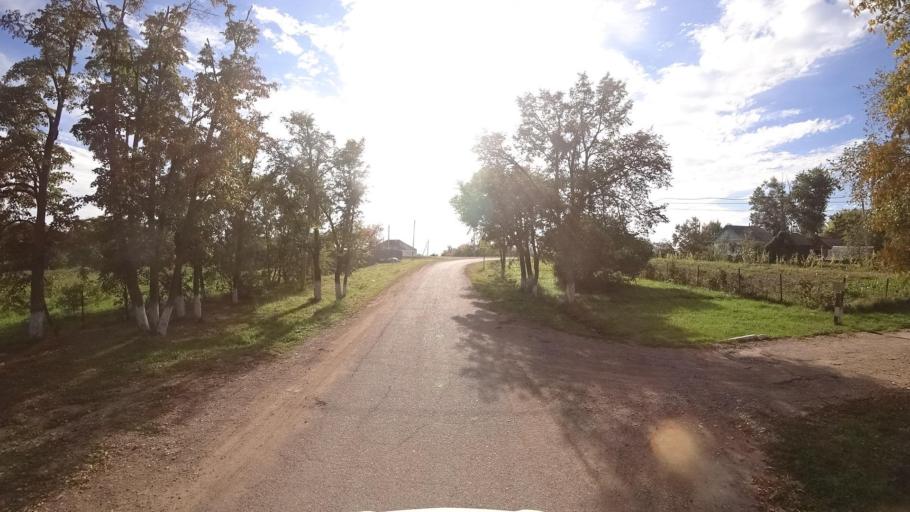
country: RU
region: Primorskiy
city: Dostoyevka
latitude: 44.2963
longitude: 133.4549
